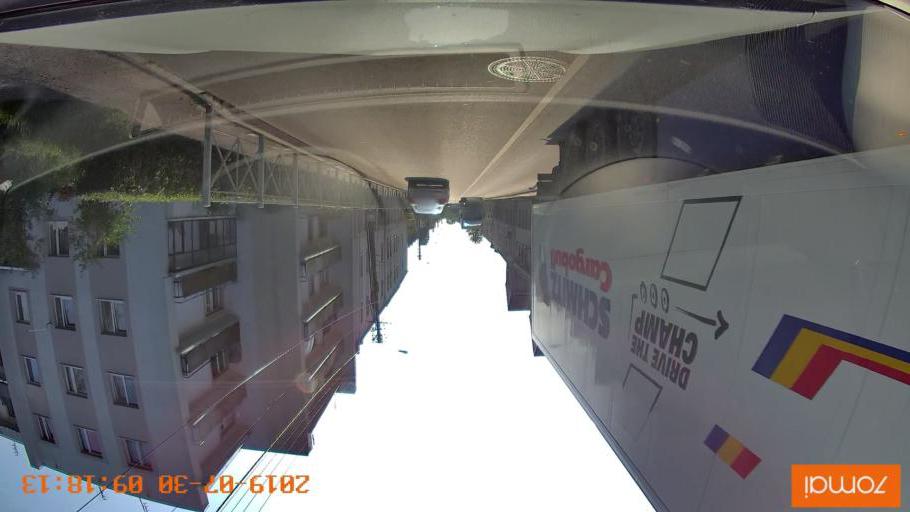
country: RU
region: Kaliningrad
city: Nesterov
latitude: 54.6309
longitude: 22.5738
